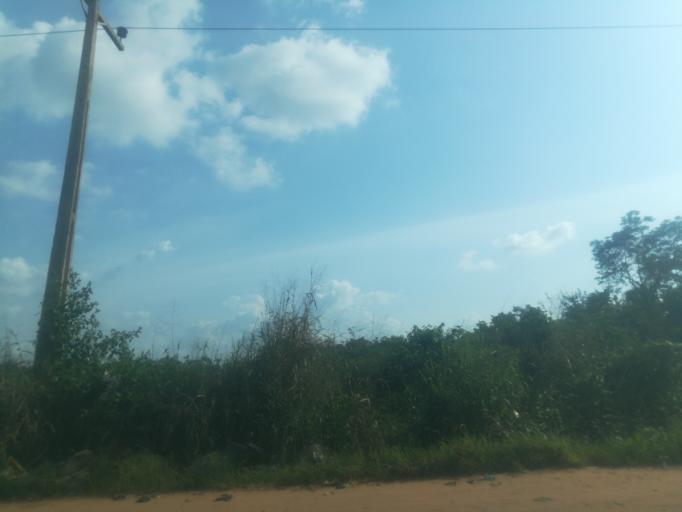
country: NG
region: Oyo
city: Ido
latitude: 7.3958
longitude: 3.7821
